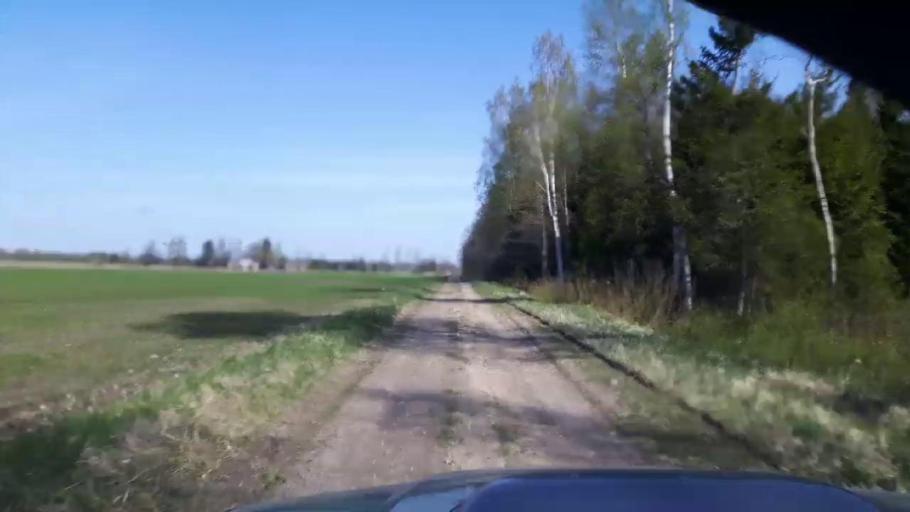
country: EE
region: Paernumaa
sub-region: Tootsi vald
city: Tootsi
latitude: 58.4768
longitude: 24.9257
